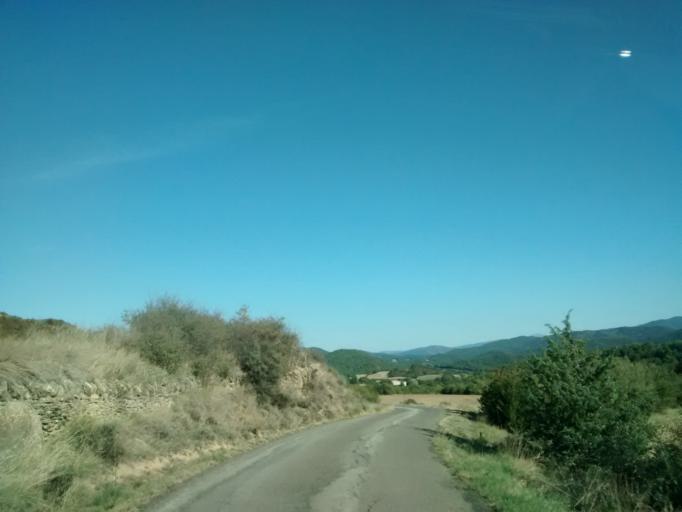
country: ES
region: Aragon
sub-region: Provincia de Huesca
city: Santa Cruz de la Seros
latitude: 42.4424
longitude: -0.6787
